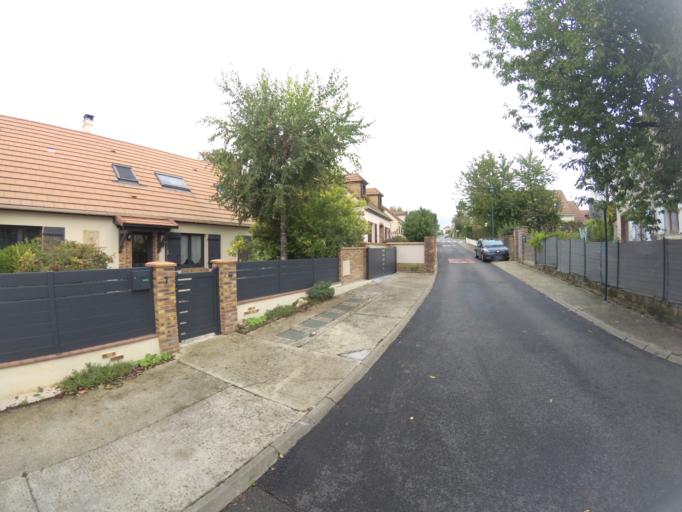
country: FR
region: Ile-de-France
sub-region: Departement de Seine-et-Marne
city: Montevrain
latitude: 48.8721
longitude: 2.7497
